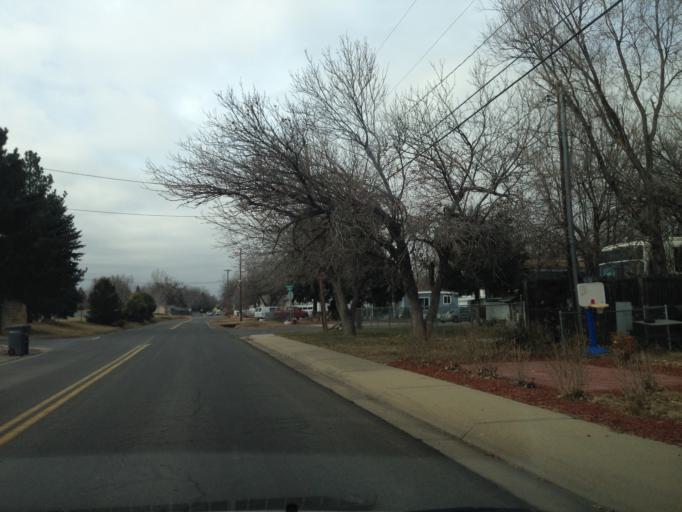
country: US
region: Colorado
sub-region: Boulder County
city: Lafayette
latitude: 39.9940
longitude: -105.0786
